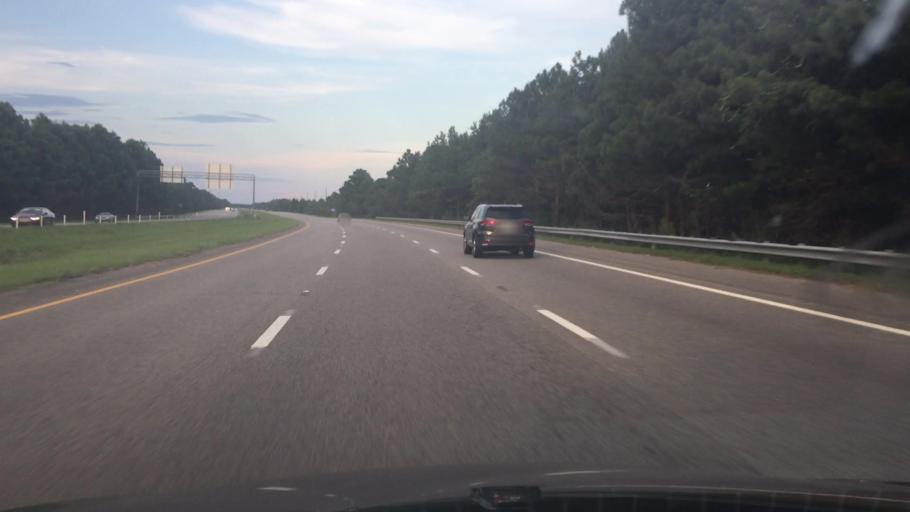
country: US
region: South Carolina
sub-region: Horry County
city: Forestbrook
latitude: 33.7428
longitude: -78.9307
